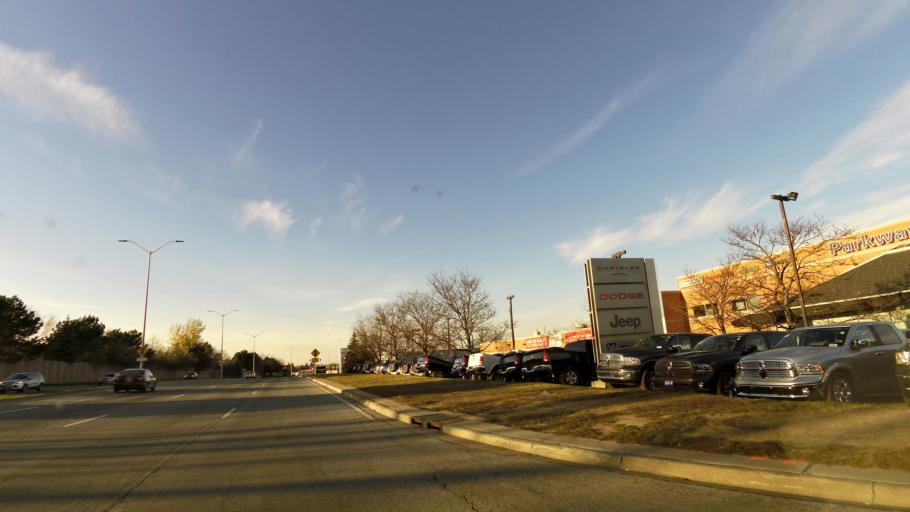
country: CA
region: Ontario
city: Mississauga
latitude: 43.5836
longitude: -79.7399
